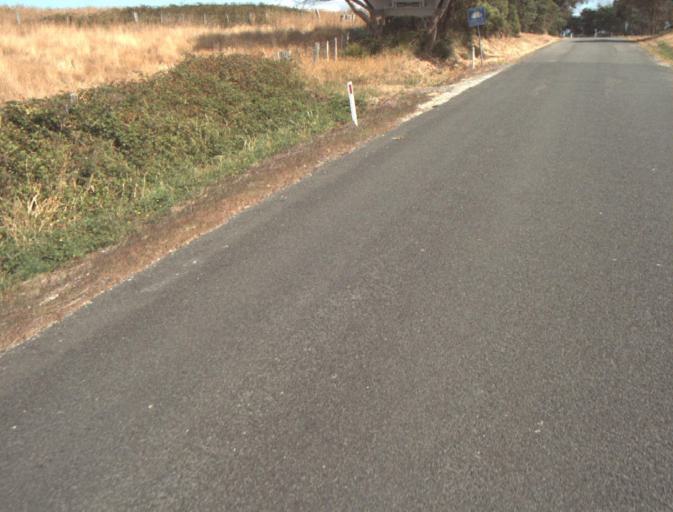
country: AU
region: Tasmania
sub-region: Launceston
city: Mayfield
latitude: -41.2051
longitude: 147.0957
